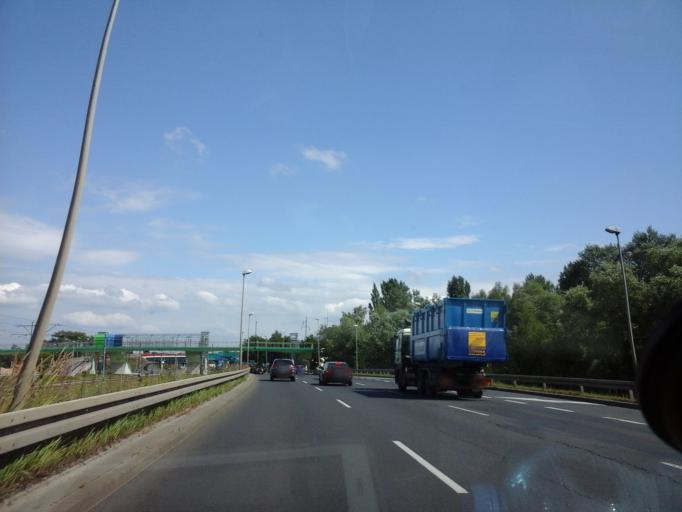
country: PL
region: West Pomeranian Voivodeship
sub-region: Szczecin
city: Szczecin
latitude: 53.3883
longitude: 14.6236
